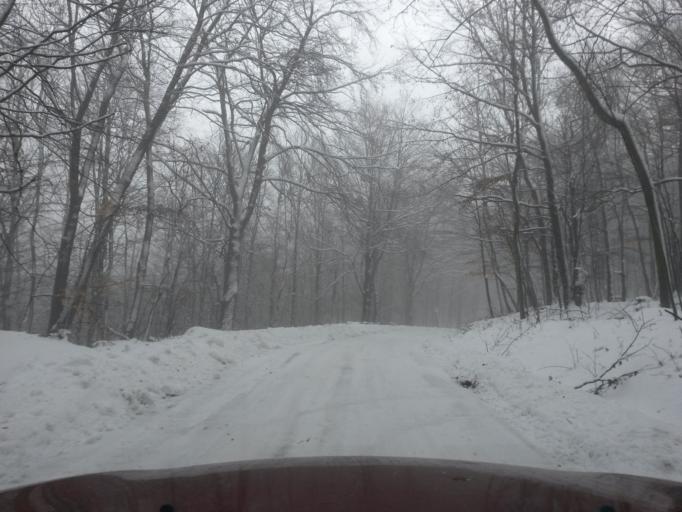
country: SK
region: Kosicky
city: Secovce
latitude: 48.8120
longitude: 21.5292
